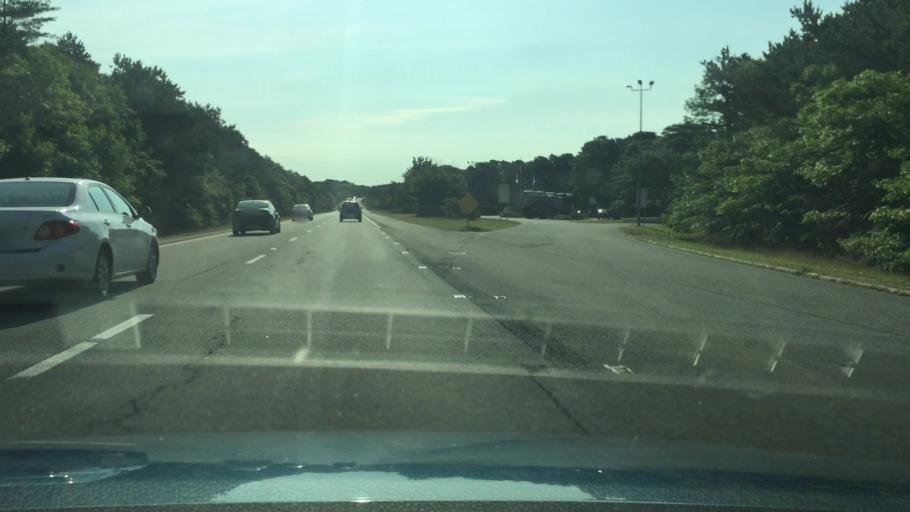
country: US
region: Massachusetts
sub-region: Barnstable County
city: Barnstable
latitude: 41.6868
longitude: -70.2901
